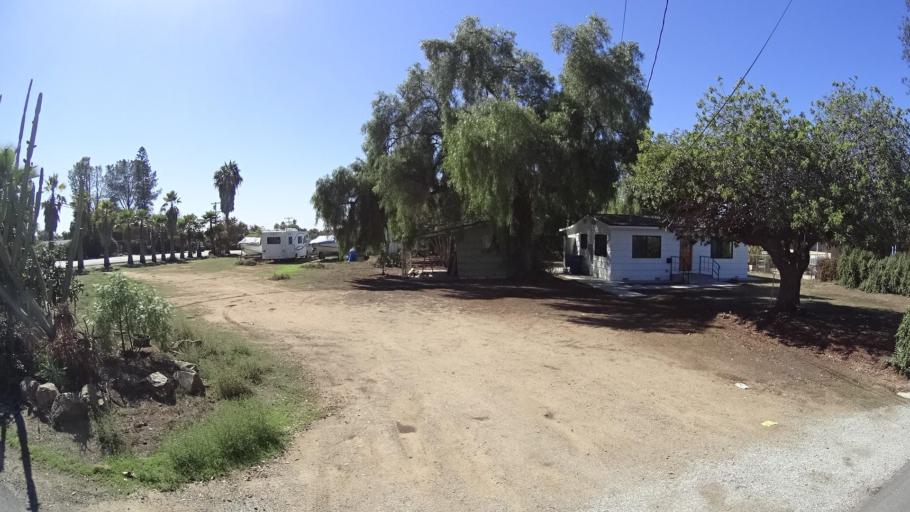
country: US
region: California
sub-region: San Diego County
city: Bonita
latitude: 32.6566
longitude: -117.0541
